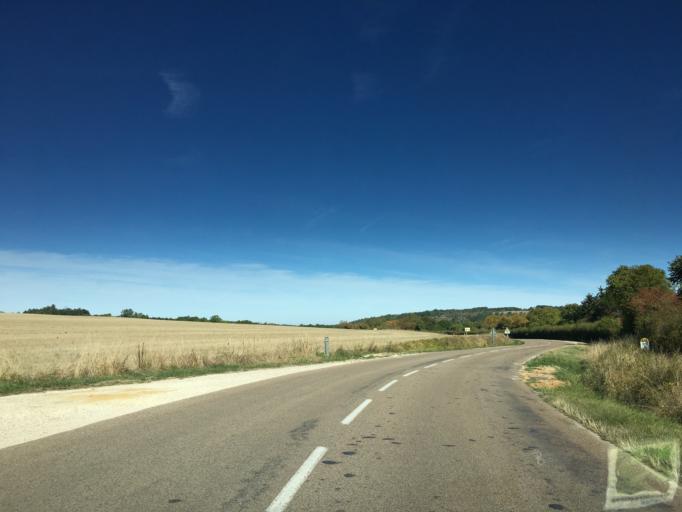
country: FR
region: Bourgogne
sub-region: Departement de l'Yonne
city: Vermenton
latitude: 47.6088
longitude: 3.6780
